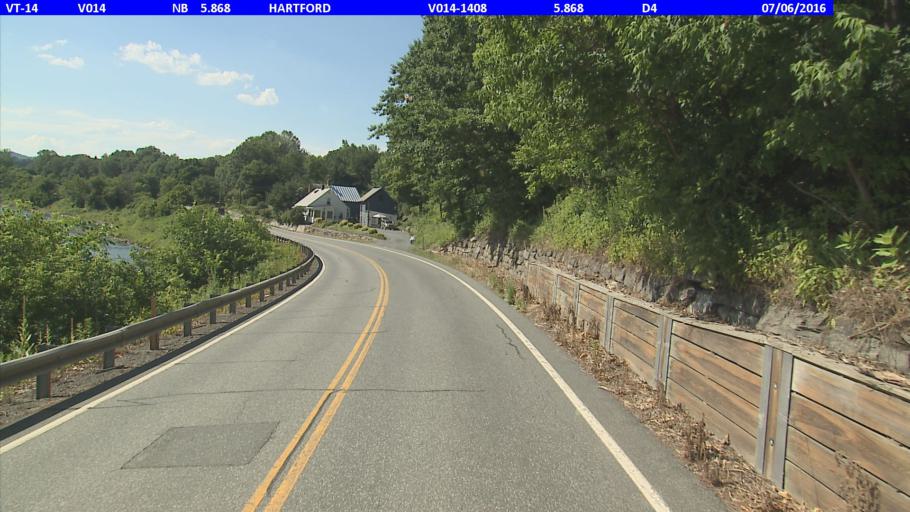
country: US
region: Vermont
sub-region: Windsor County
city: White River Junction
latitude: 43.7011
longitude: -72.4056
